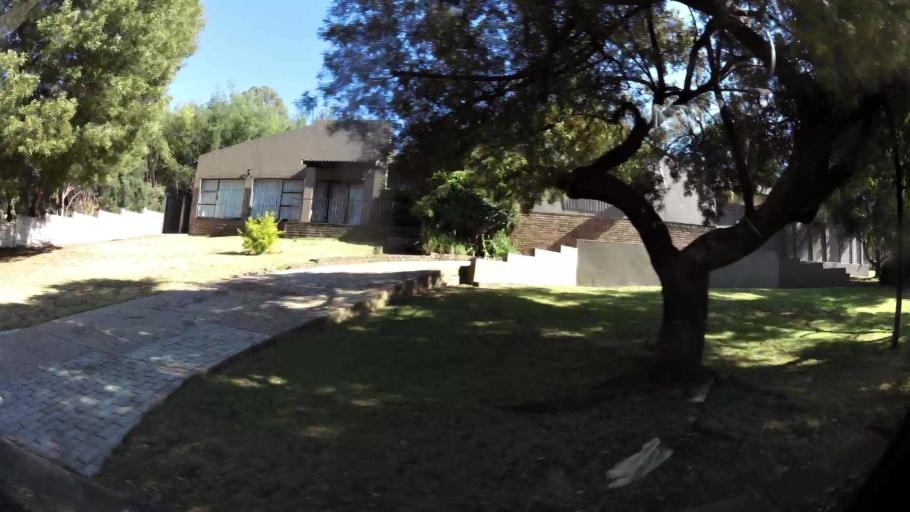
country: ZA
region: Gauteng
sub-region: City of Johannesburg Metropolitan Municipality
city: Roodepoort
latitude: -26.1189
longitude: 27.8681
